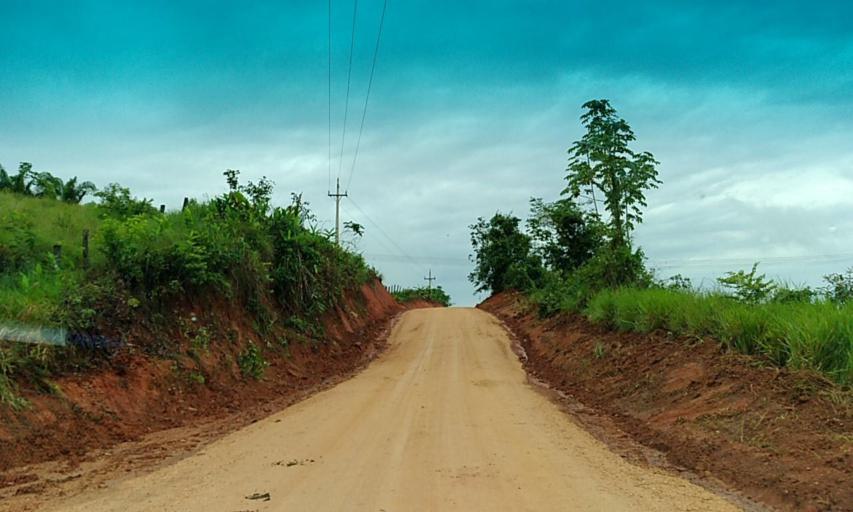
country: BR
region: Para
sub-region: Altamira
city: Altamira
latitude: -3.1030
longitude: -51.6341
